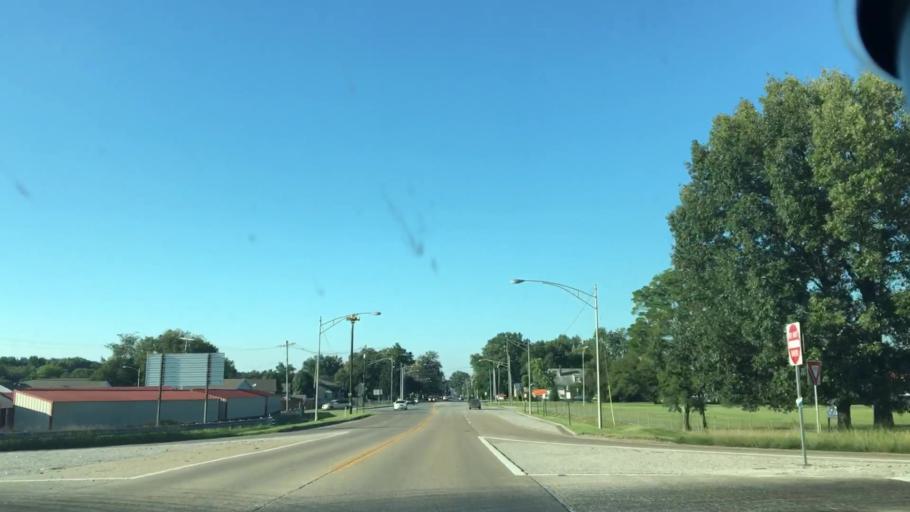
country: US
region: Indiana
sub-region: Vanderburgh County
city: Evansville
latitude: 37.9406
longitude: -87.4925
